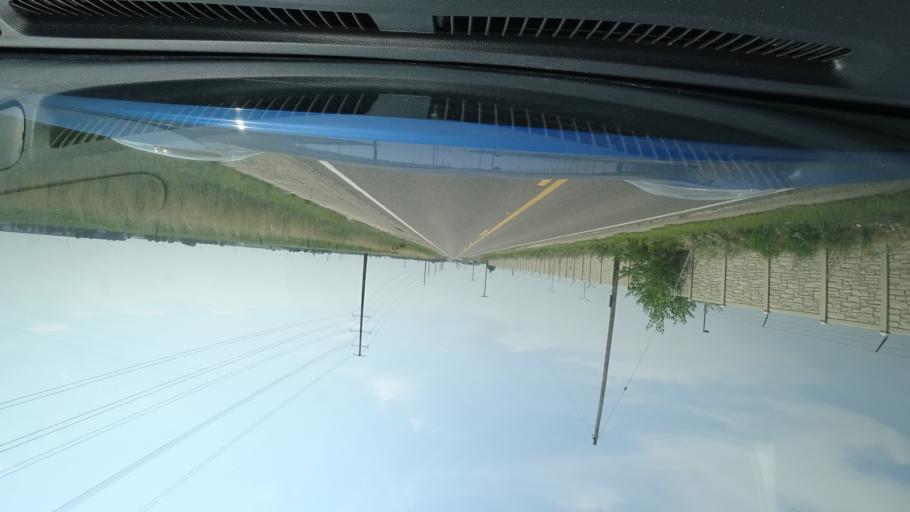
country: US
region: Colorado
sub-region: Adams County
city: Aurora
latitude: 39.7647
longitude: -104.7346
